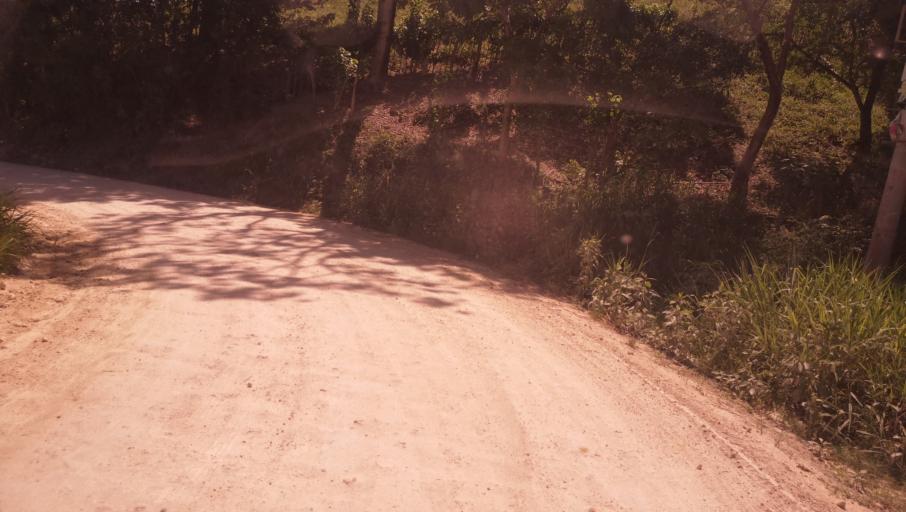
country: GT
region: Peten
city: Melchor de Mencos
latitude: 16.9855
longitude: -89.2562
